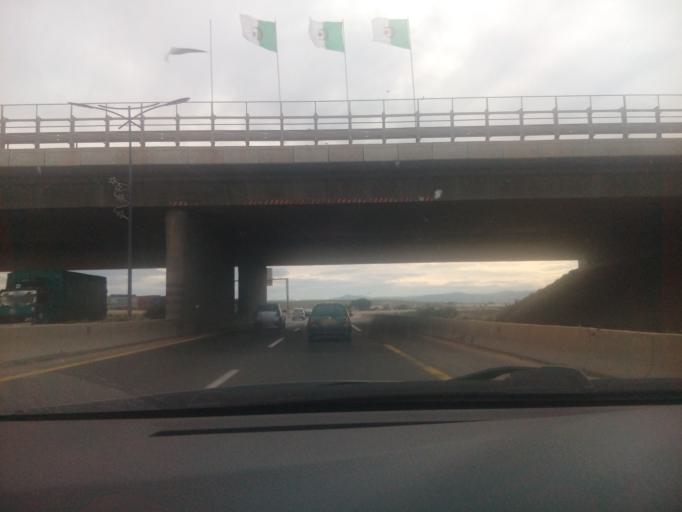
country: DZ
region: Oran
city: Es Senia
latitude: 35.6018
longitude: -0.5747
